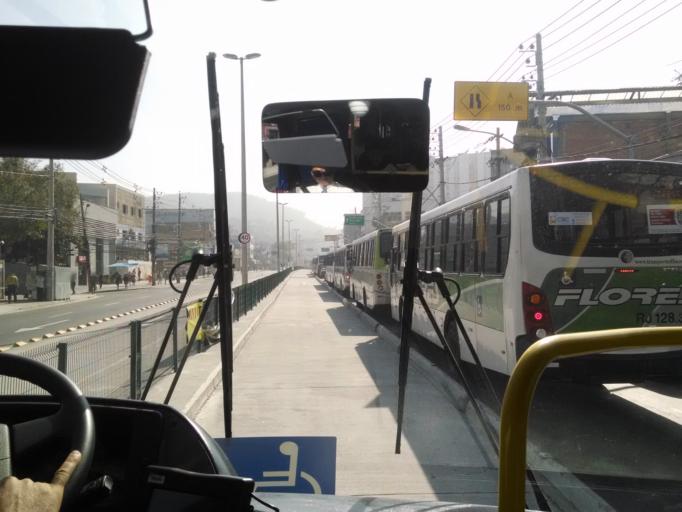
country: BR
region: Rio de Janeiro
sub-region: Sao Joao De Meriti
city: Sao Joao de Meriti
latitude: -22.8689
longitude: -43.3351
